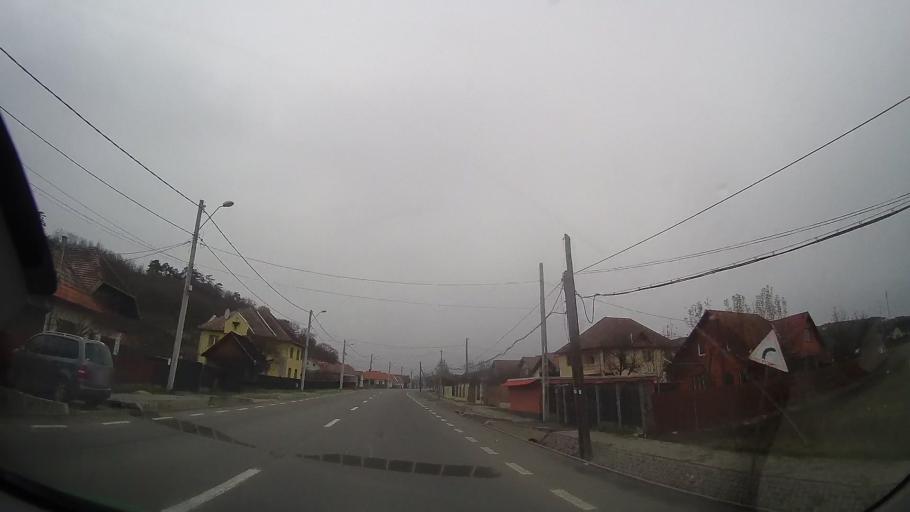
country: RO
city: Remetea
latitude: 46.5965
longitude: 24.5317
